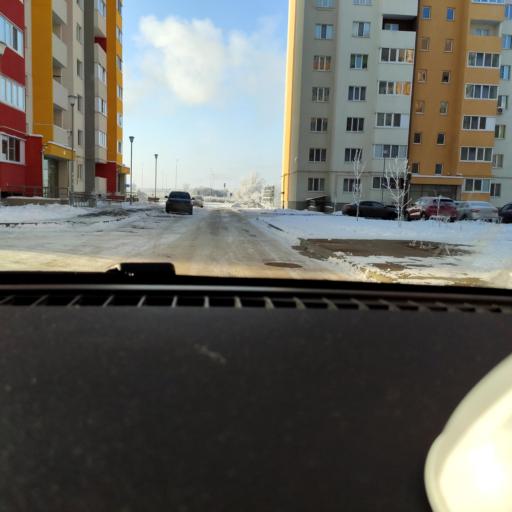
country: RU
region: Samara
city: Samara
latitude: 53.0923
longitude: 50.1607
